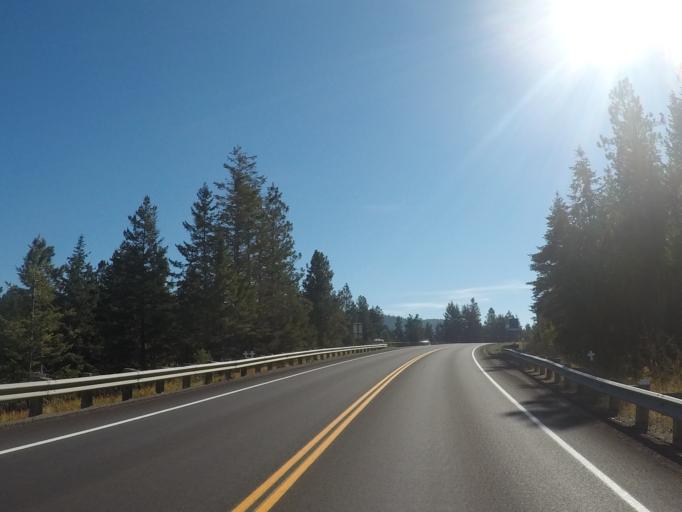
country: US
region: Montana
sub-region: Lake County
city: Polson
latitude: 47.8060
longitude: -114.2382
